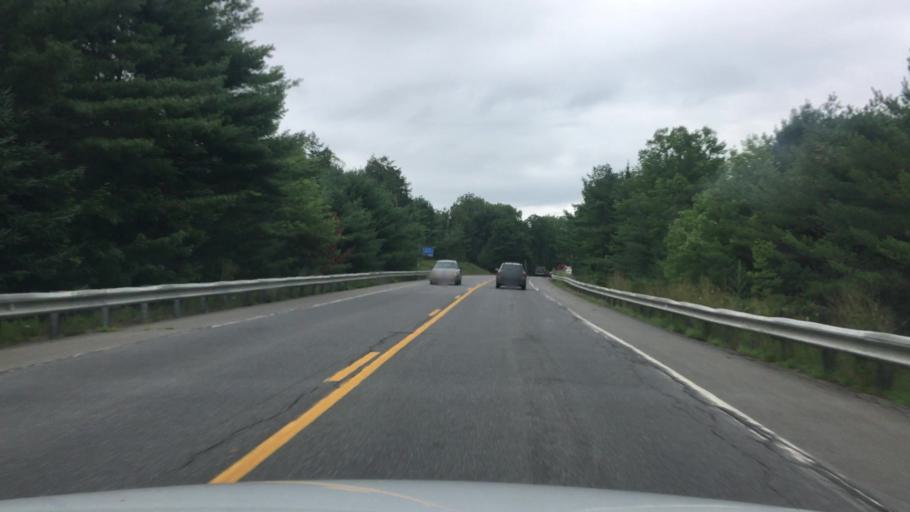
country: US
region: Maine
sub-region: Penobscot County
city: Bradley
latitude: 44.8263
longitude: -68.3933
